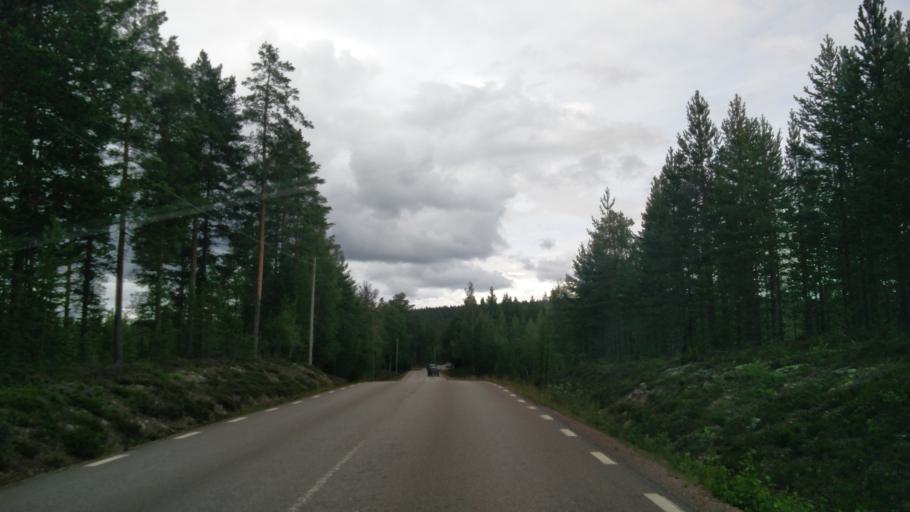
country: NO
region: Hedmark
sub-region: Trysil
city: Innbygda
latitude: 61.1733
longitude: 12.8469
